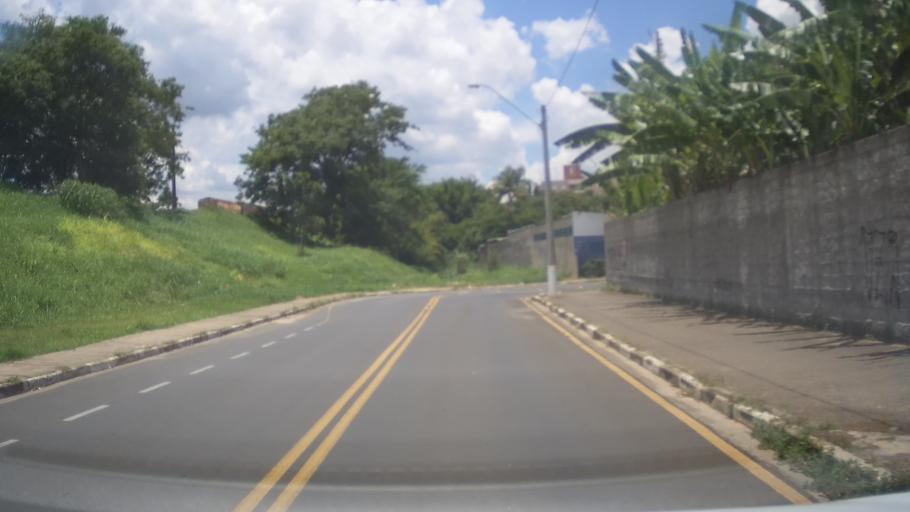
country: BR
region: Sao Paulo
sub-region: Vinhedo
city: Vinhedo
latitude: -23.0319
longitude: -46.9699
